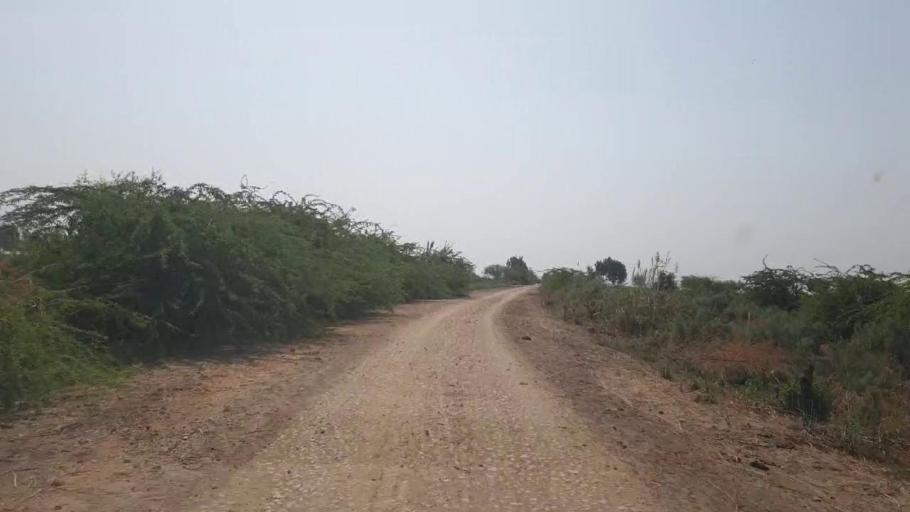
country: PK
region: Sindh
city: Jati
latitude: 24.3813
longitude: 68.6020
